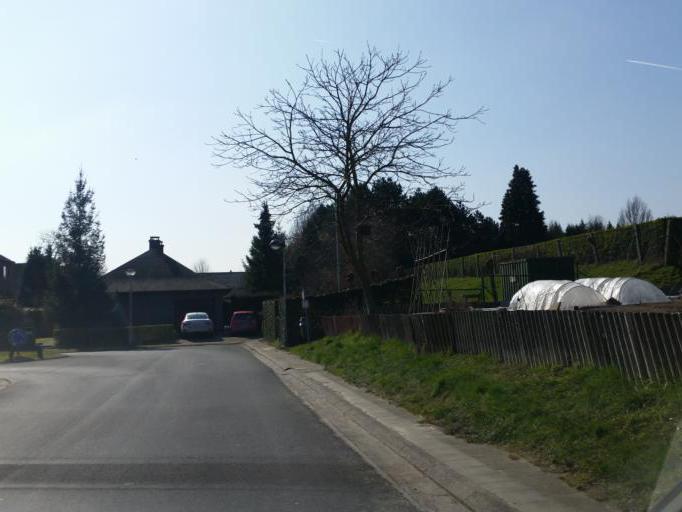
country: BE
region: Flanders
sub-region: Provincie Oost-Vlaanderen
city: Kruibeke
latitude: 51.1655
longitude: 4.3117
